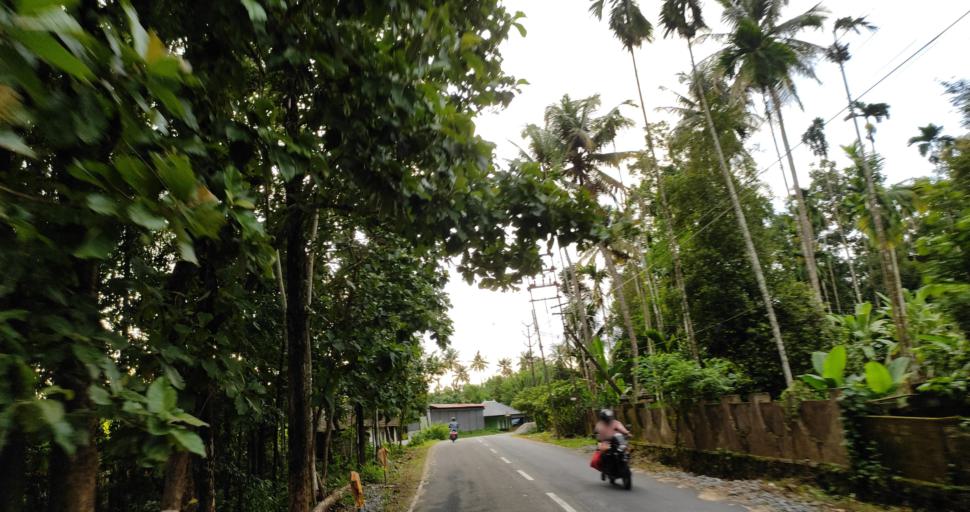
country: IN
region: Kerala
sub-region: Thrissur District
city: Kizhake Chalakudi
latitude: 10.3121
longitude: 76.3895
